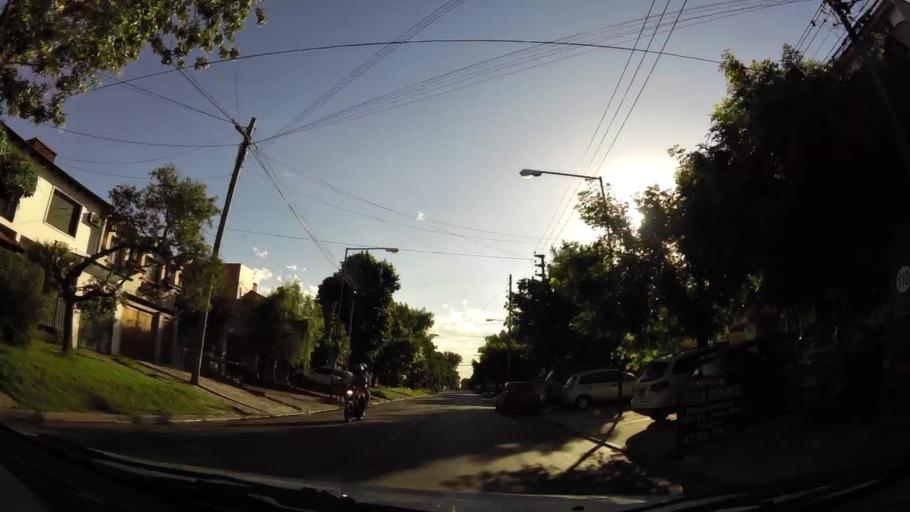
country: AR
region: Buenos Aires
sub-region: Partido de San Isidro
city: San Isidro
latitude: -34.4794
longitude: -58.5335
